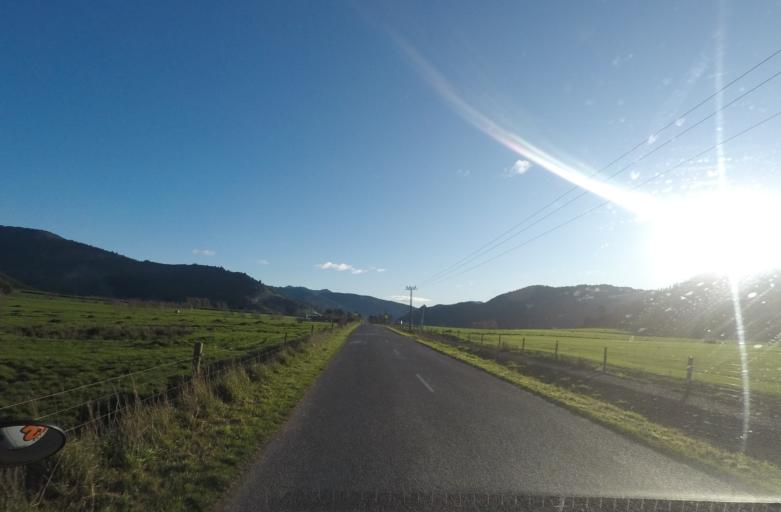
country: NZ
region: Marlborough
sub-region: Marlborough District
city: Picton
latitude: -41.2896
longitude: 173.8776
